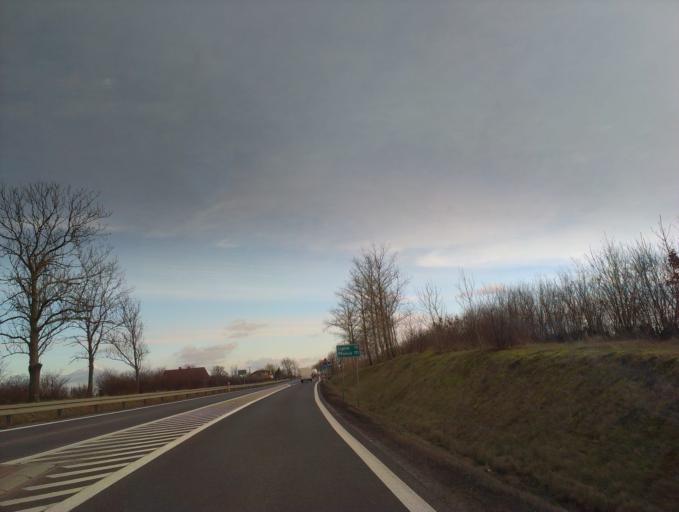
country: PL
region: Kujawsko-Pomorskie
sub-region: Powiat torunski
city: Czernikowo
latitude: 52.9329
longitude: 19.0183
